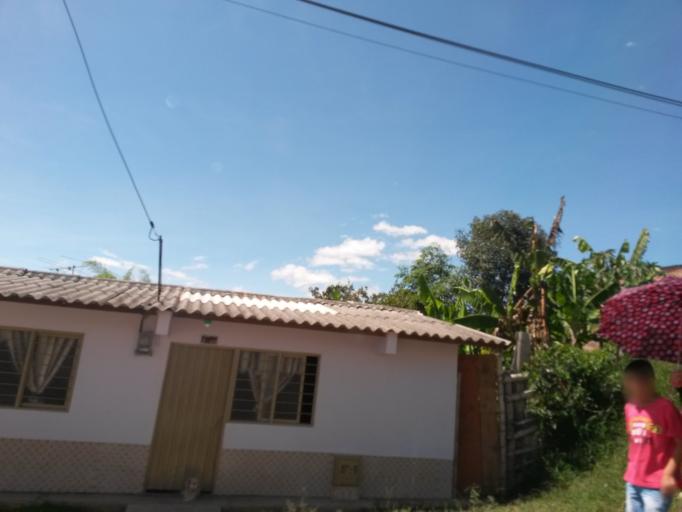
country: CO
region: Cauca
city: El Tambo
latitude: 2.4537
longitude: -76.8121
